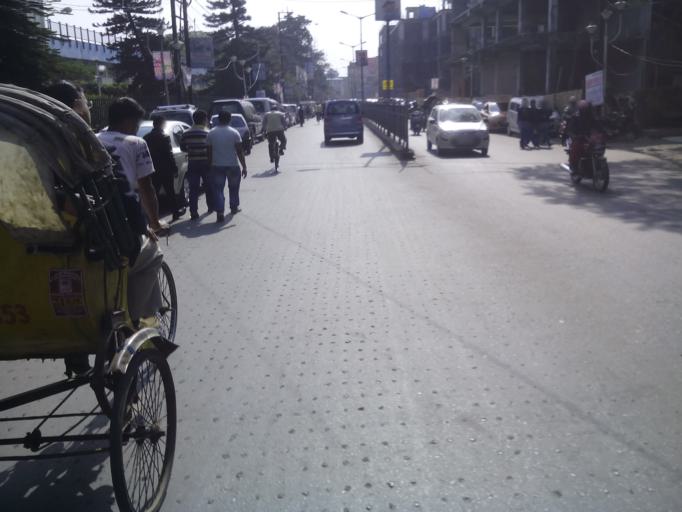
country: IN
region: West Bengal
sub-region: Darjiling
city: Shiliguri
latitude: 26.7137
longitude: 88.4262
